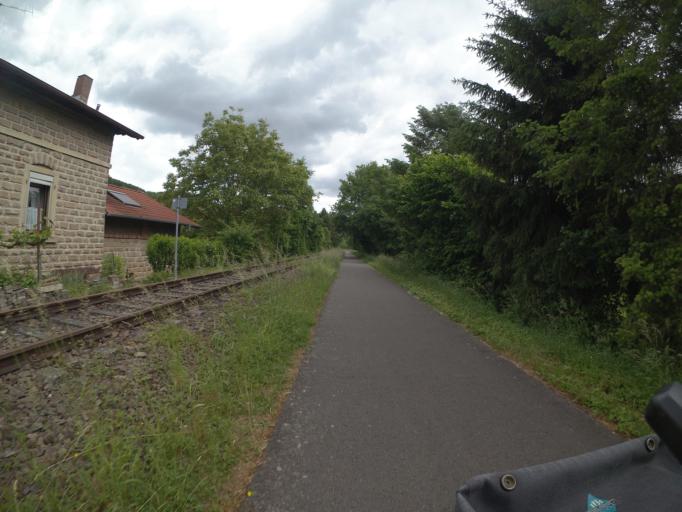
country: DE
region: Rheinland-Pfalz
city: Sankt Julian
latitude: 49.6082
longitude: 7.5140
